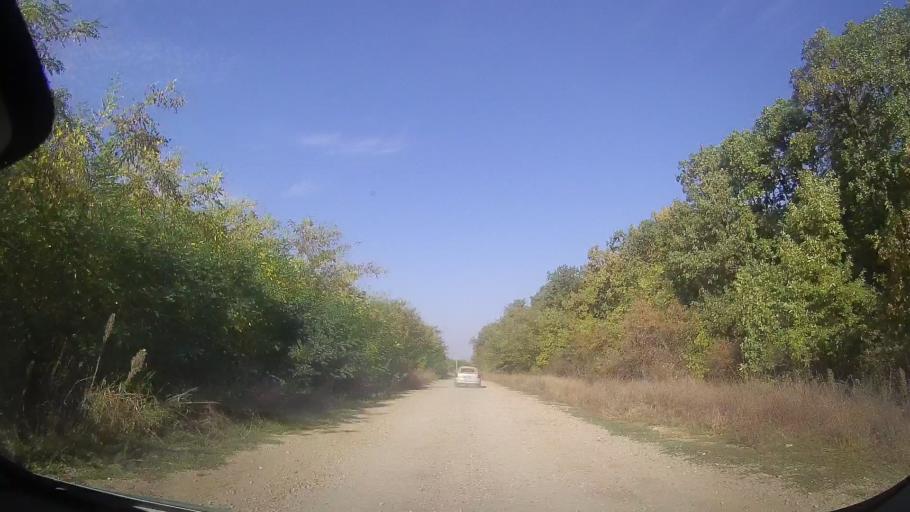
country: RO
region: Timis
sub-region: Oras Recas
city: Recas
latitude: 45.8773
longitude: 21.5215
